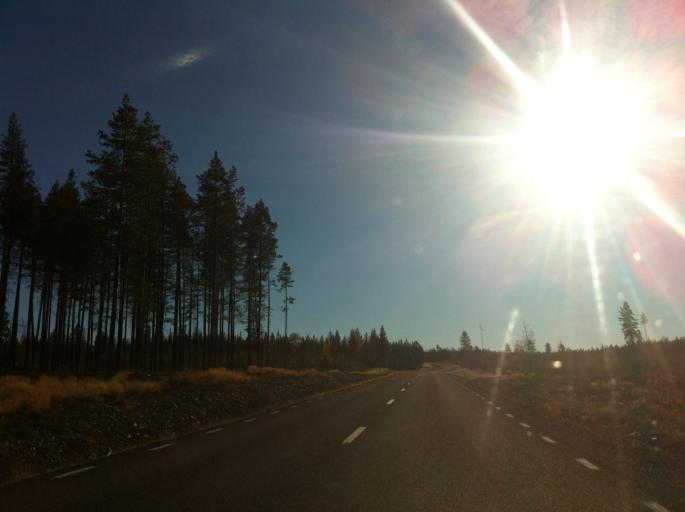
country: SE
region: Dalarna
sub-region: Alvdalens Kommun
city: AElvdalen
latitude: 61.6281
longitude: 13.2320
